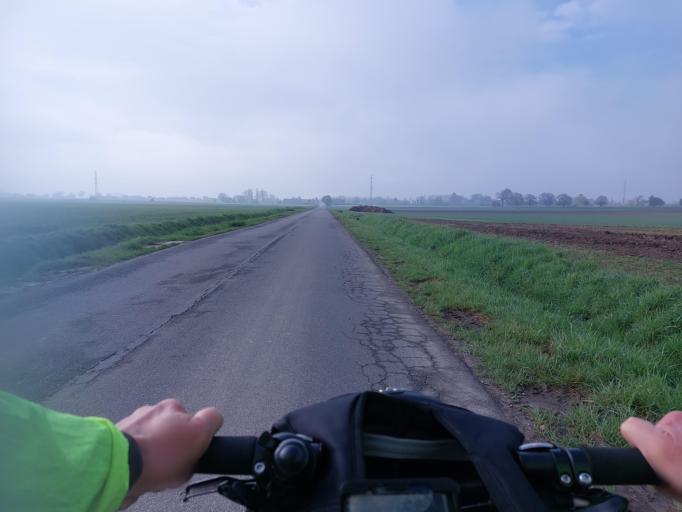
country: BE
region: Wallonia
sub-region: Province du Hainaut
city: Estinnes-au-Val
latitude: 50.4404
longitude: 4.0504
